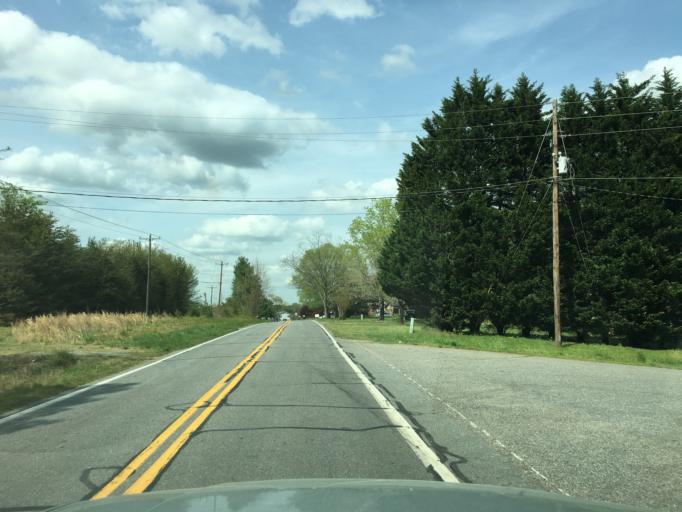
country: US
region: North Carolina
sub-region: Rutherford County
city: Spindale
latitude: 35.3043
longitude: -81.9388
